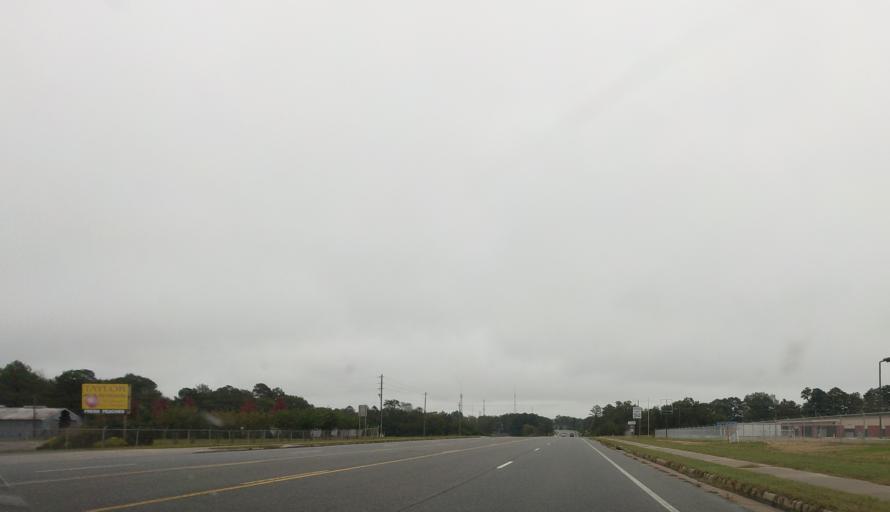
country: US
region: Georgia
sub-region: Taylor County
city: Reynolds
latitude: 32.5606
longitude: -84.1073
